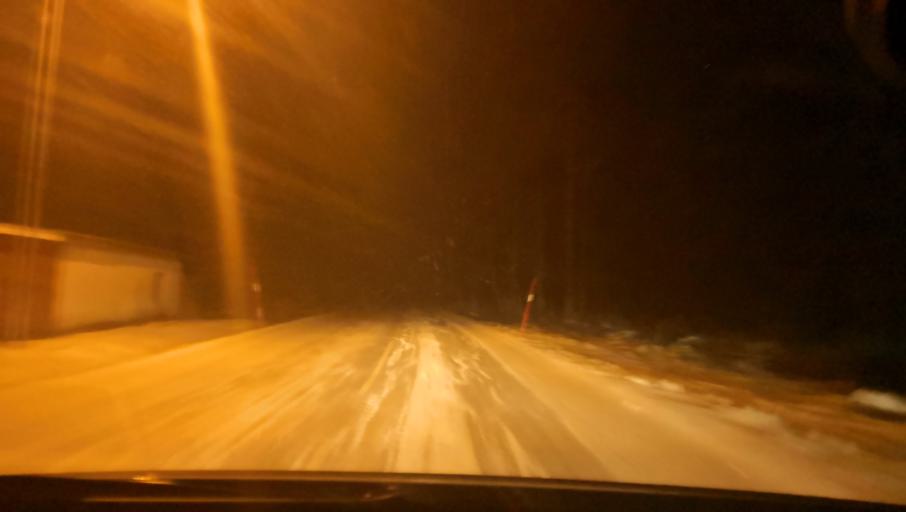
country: SE
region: Uppsala
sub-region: Heby Kommun
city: Tarnsjo
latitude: 60.1438
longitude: 16.9107
